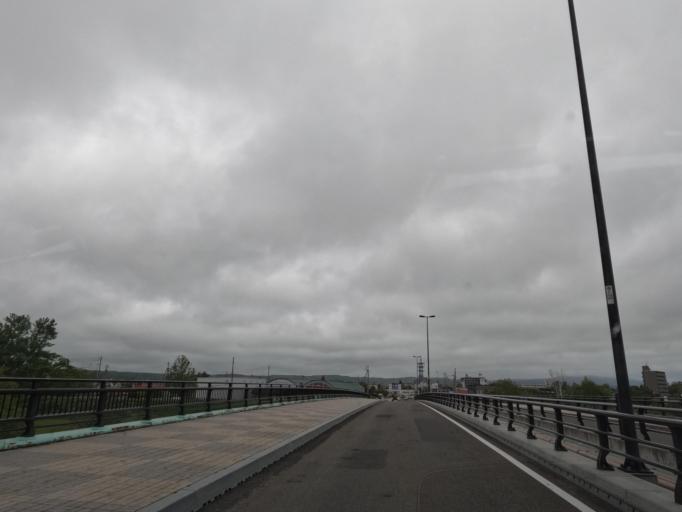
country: JP
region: Hokkaido
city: Tobetsu
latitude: 43.2133
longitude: 141.5175
